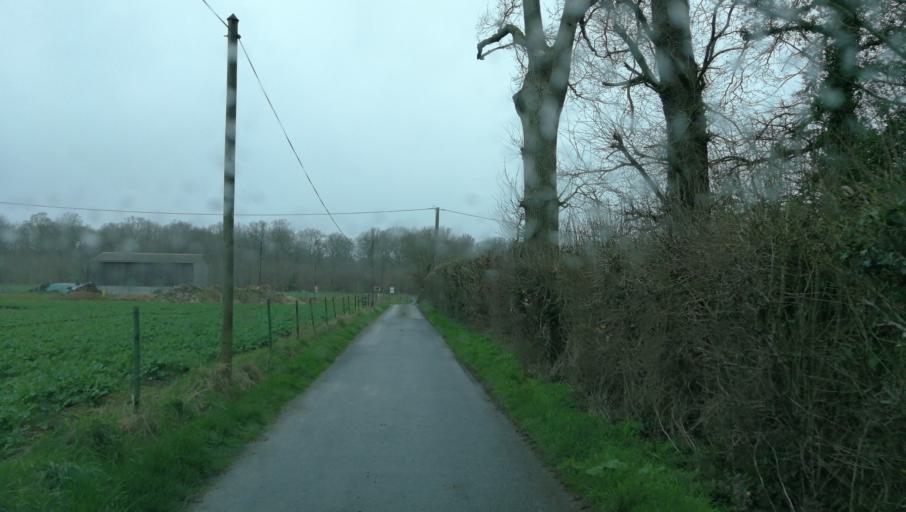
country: FR
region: Haute-Normandie
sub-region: Departement de l'Eure
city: Brionne
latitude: 49.1783
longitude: 0.6986
